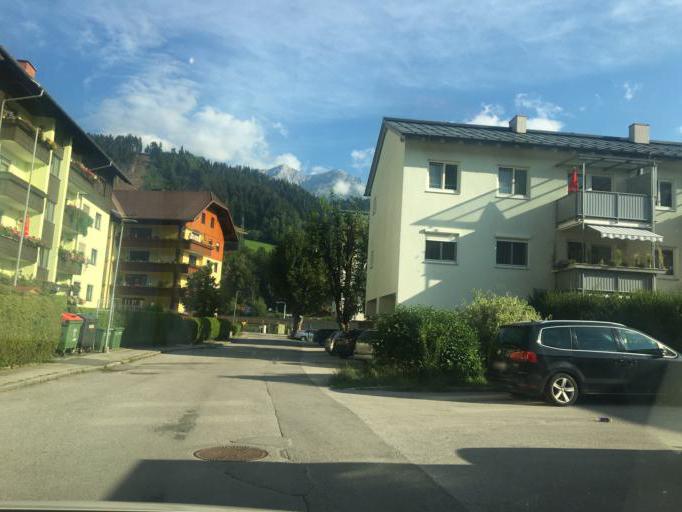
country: AT
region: Styria
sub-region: Politischer Bezirk Liezen
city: Schladming
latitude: 47.3980
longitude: 13.6991
